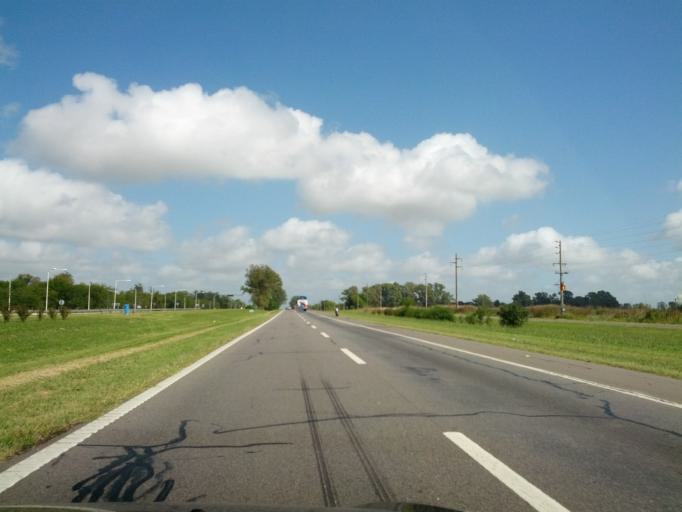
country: AR
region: Buenos Aires
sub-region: Partido de Mercedes
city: Mercedes
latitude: -34.6472
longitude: -59.3065
